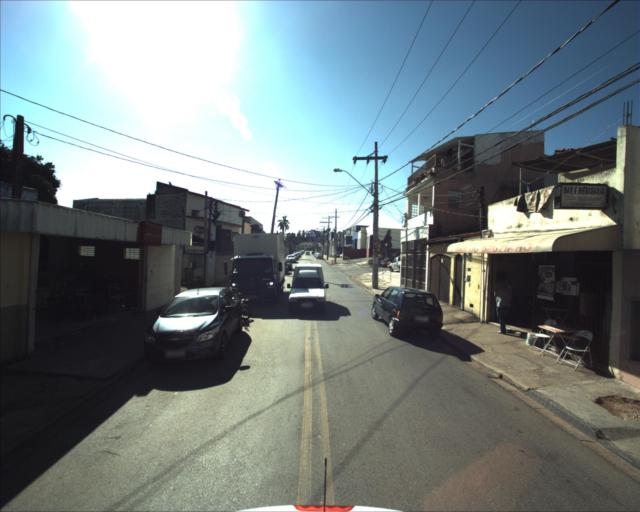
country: BR
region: Sao Paulo
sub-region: Sorocaba
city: Sorocaba
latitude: -23.4651
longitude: -47.4421
